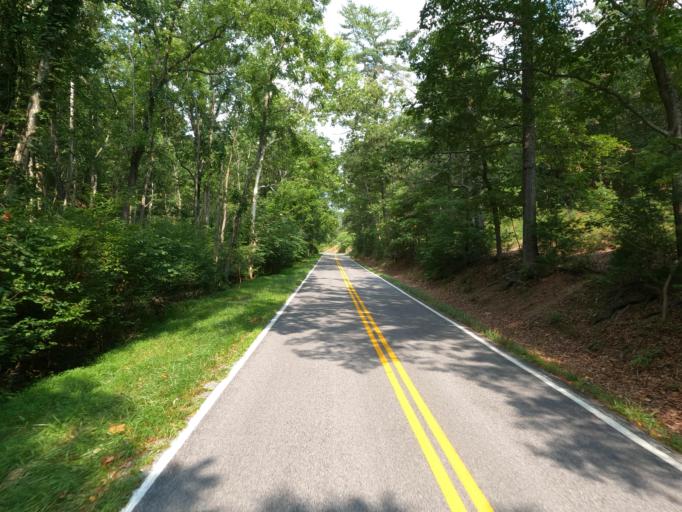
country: US
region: West Virginia
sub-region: Morgan County
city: Berkeley Springs
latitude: 39.6766
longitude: -78.2663
